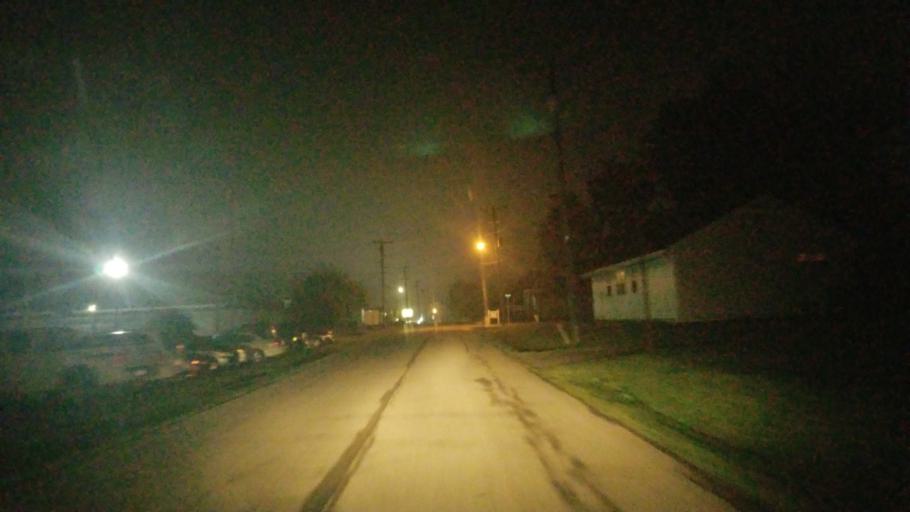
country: US
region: Missouri
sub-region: Pike County
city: Bowling Green
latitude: 39.3412
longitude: -91.1989
